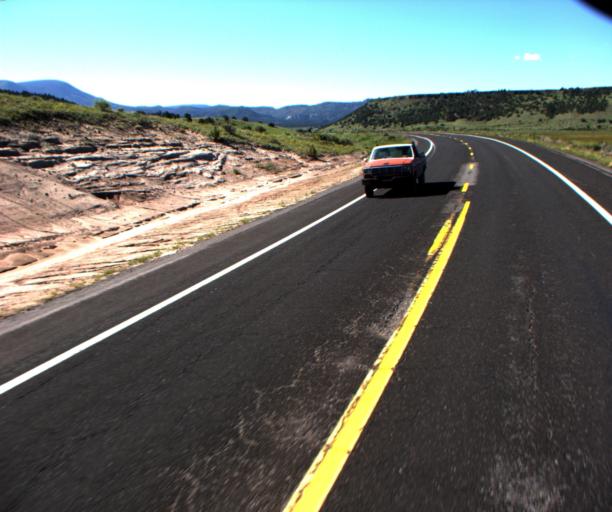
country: US
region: Arizona
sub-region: Apache County
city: Eagar
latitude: 34.0422
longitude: -109.1873
